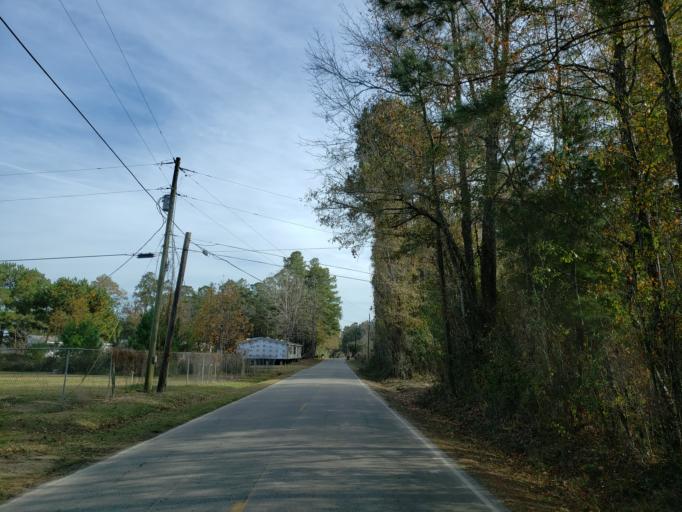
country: US
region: Mississippi
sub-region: Forrest County
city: Rawls Springs
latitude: 31.3950
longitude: -89.3867
